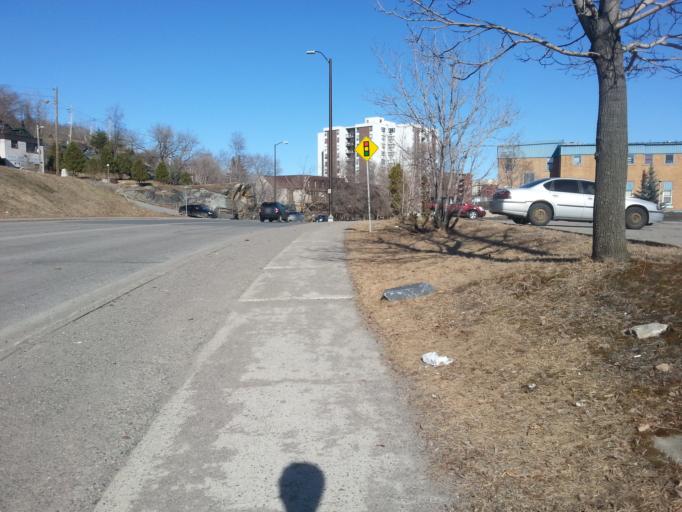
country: CA
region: Ontario
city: Greater Sudbury
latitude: 46.4953
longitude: -80.9950
